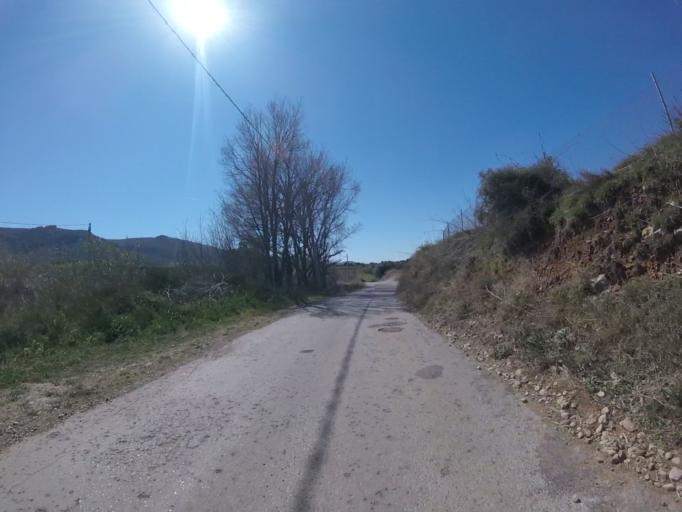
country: ES
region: Valencia
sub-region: Provincia de Castello
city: Chert/Xert
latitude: 40.4132
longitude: 0.1748
